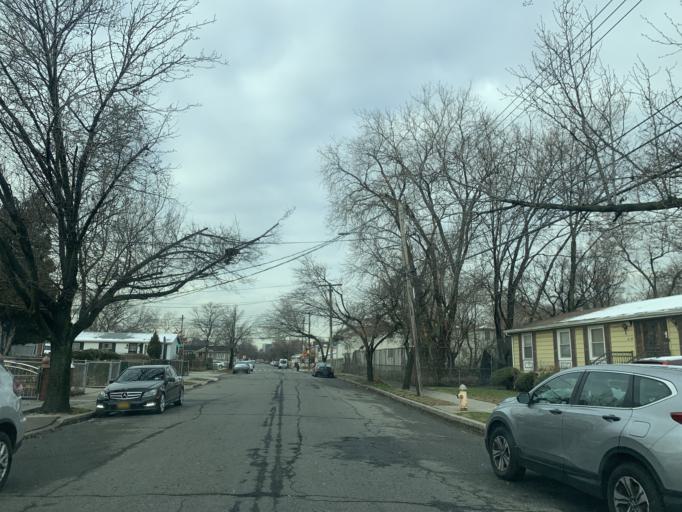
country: US
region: New York
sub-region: Queens County
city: Jamaica
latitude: 40.6885
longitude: -73.7930
